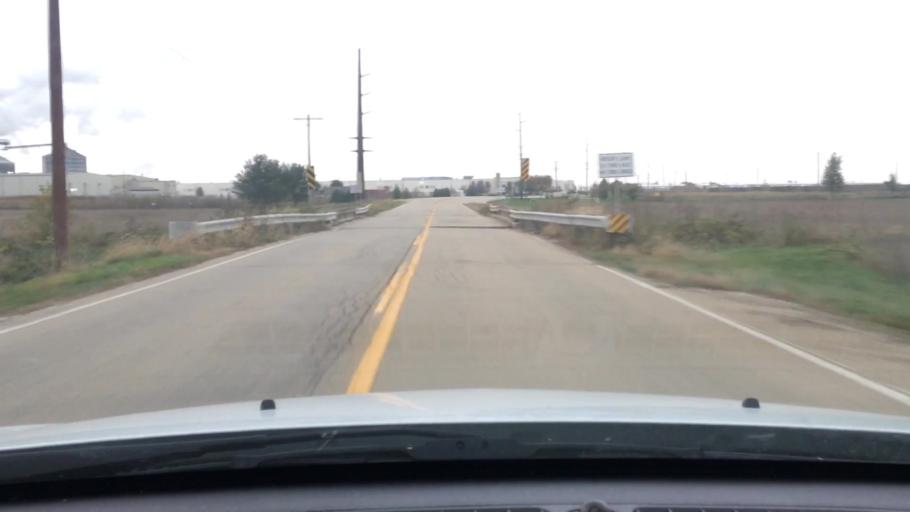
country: US
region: Illinois
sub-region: Ogle County
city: Rochelle
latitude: 41.8897
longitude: -89.0281
